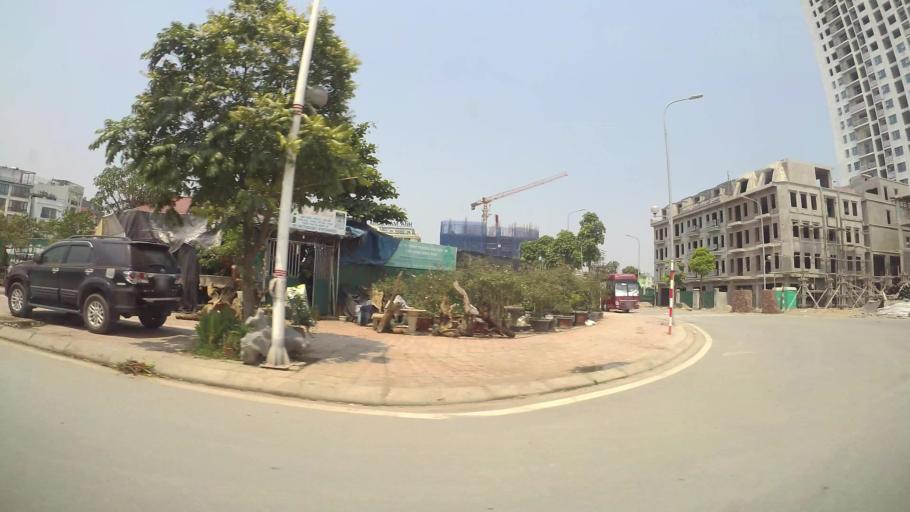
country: VN
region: Ha Noi
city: Hoan Kiem
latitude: 21.0394
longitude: 105.8754
